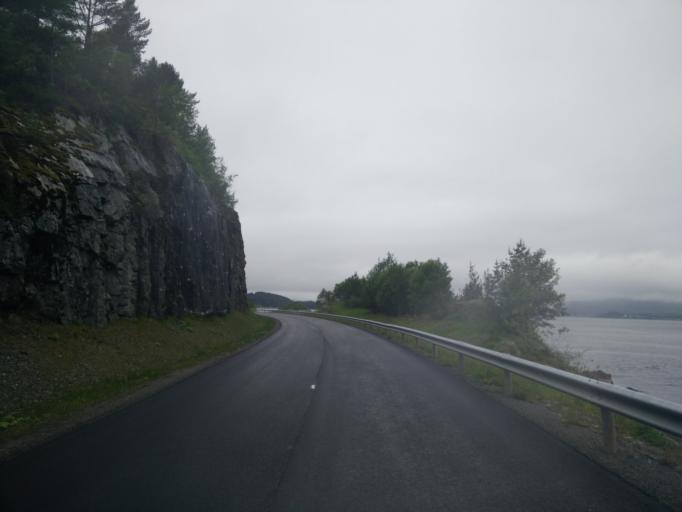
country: NO
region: More og Romsdal
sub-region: Kristiansund
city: Rensvik
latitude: 62.9932
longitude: 7.8960
